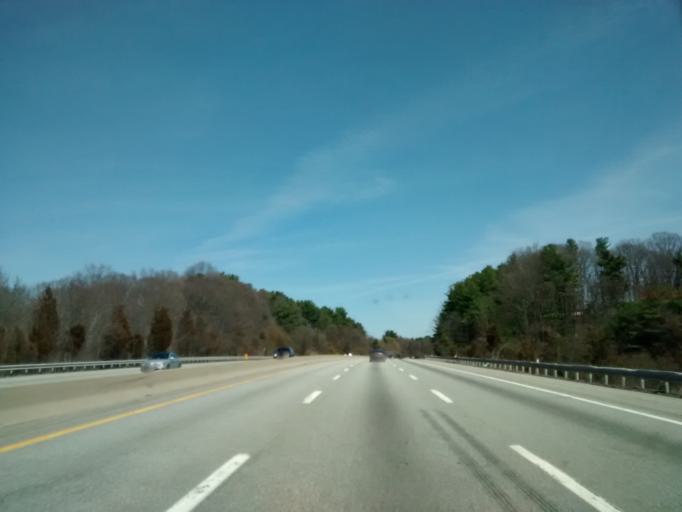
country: US
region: Massachusetts
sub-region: Middlesex County
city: Framingham Center
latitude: 42.3152
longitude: -71.4129
